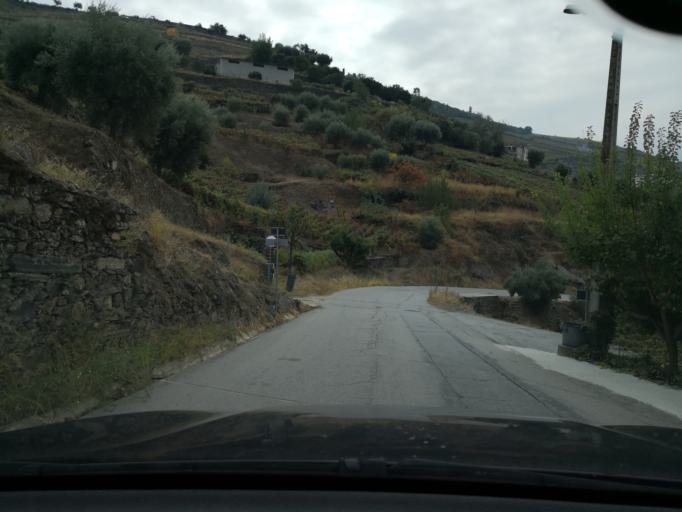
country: PT
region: Vila Real
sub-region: Peso da Regua
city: Peso da Regua
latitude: 41.1739
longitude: -7.7441
